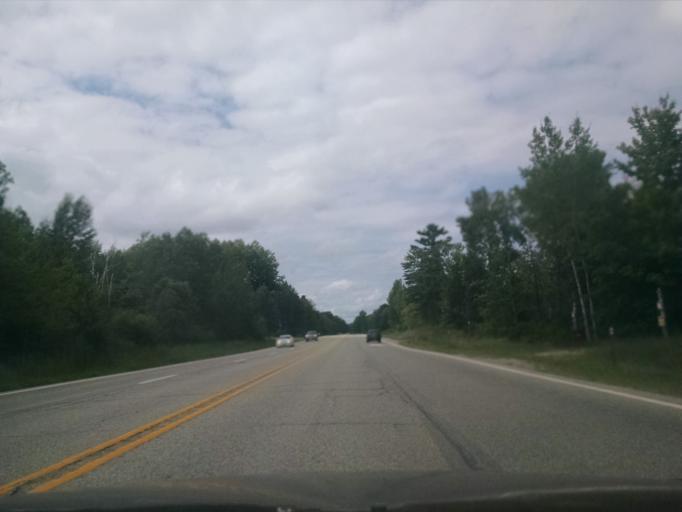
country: US
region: Michigan
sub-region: Osceola County
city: Evart
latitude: 44.0541
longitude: -85.1814
